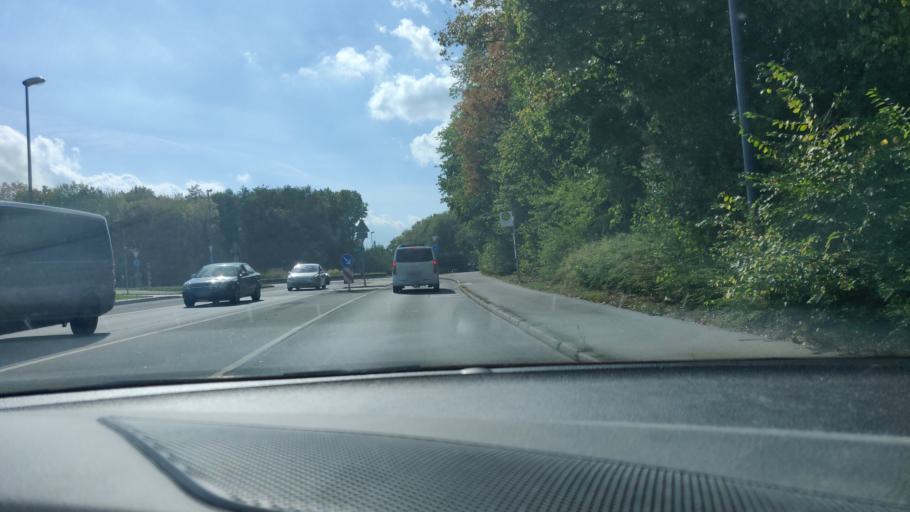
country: DE
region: North Rhine-Westphalia
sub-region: Regierungsbezirk Dusseldorf
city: Velbert
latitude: 51.3421
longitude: 7.0587
